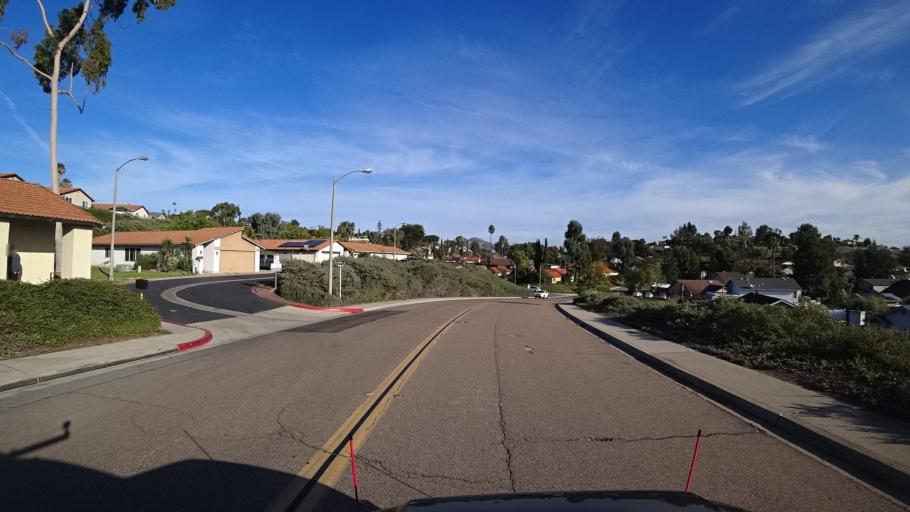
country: US
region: California
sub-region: San Diego County
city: Spring Valley
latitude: 32.7334
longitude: -116.9811
